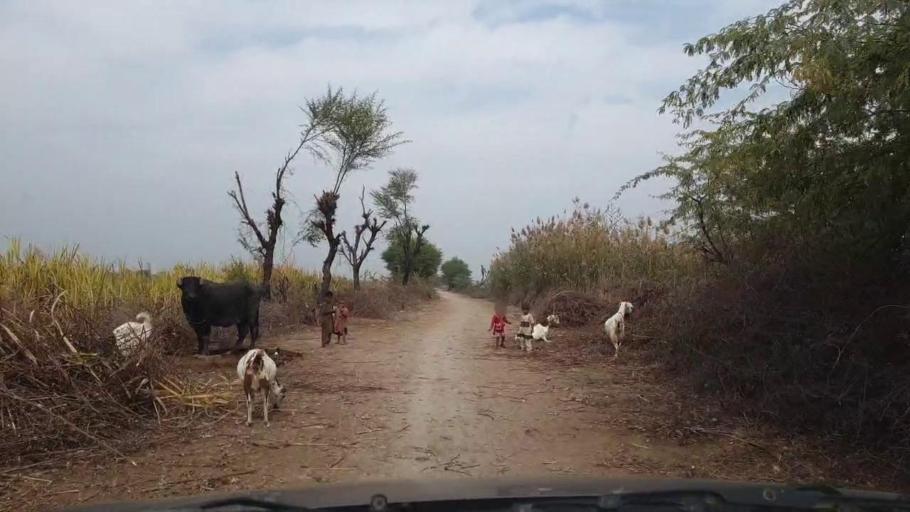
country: PK
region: Sindh
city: Sinjhoro
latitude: 26.0728
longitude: 68.8285
